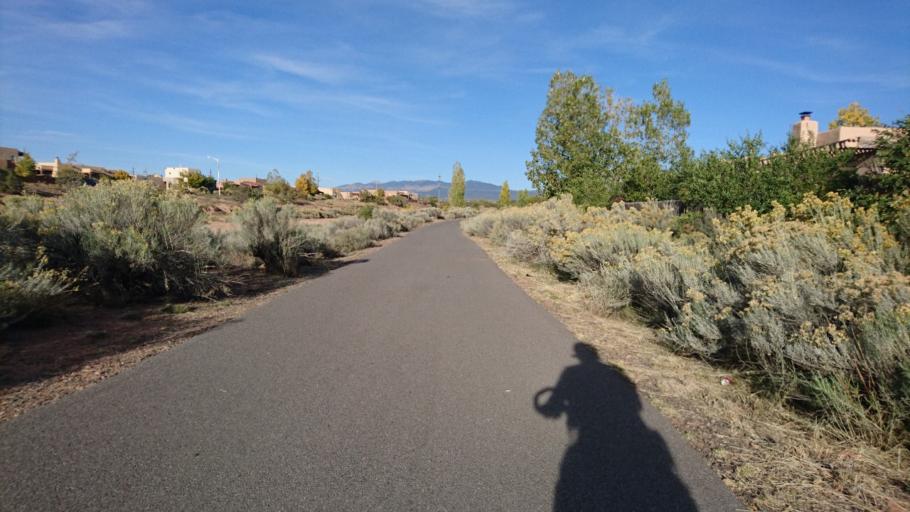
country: US
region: New Mexico
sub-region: Santa Fe County
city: Agua Fria
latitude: 35.6422
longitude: -106.0027
